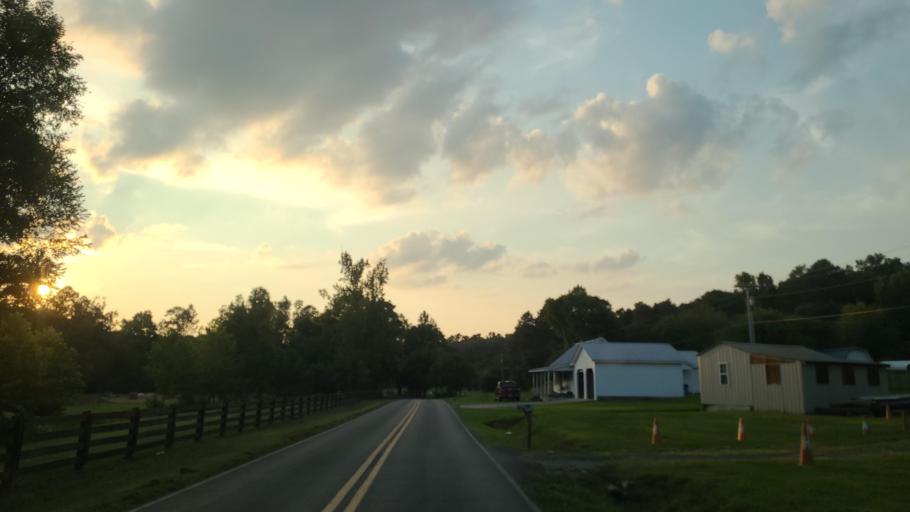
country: US
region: Georgia
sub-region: Bartow County
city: Adairsville
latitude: 34.4324
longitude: -84.8936
